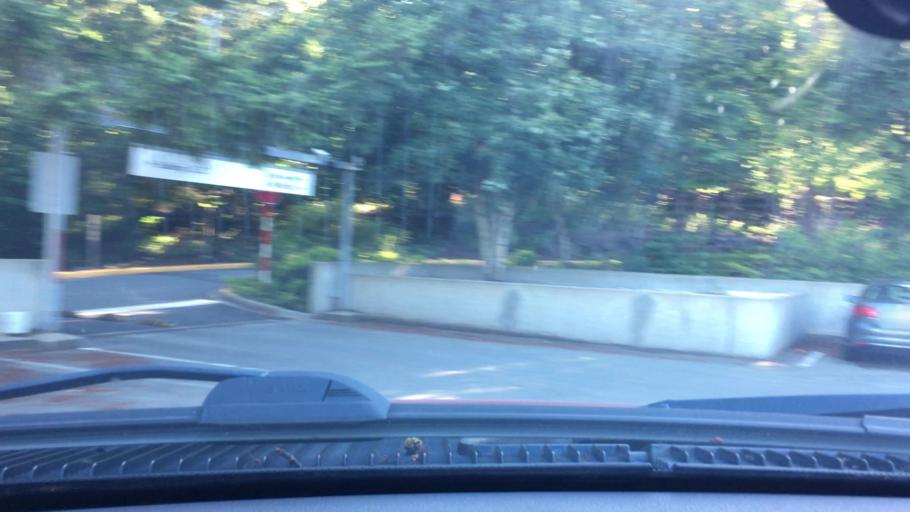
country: US
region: Washington
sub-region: King County
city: Redmond
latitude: 47.6423
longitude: -122.1227
